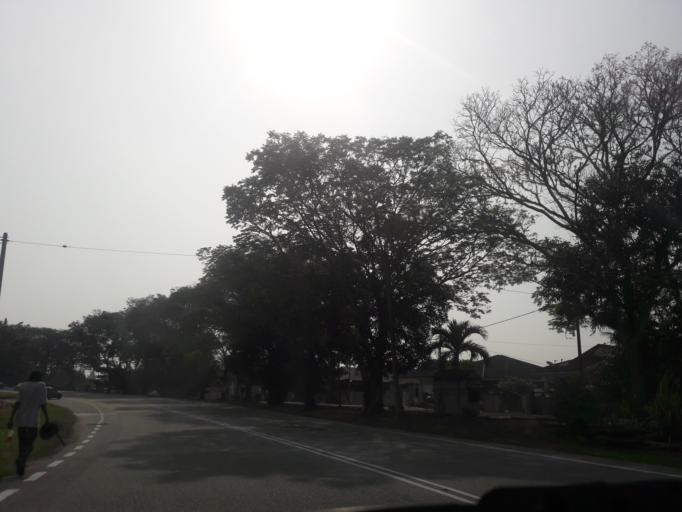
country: MY
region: Kedah
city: Kulim
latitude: 5.3468
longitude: 100.5221
